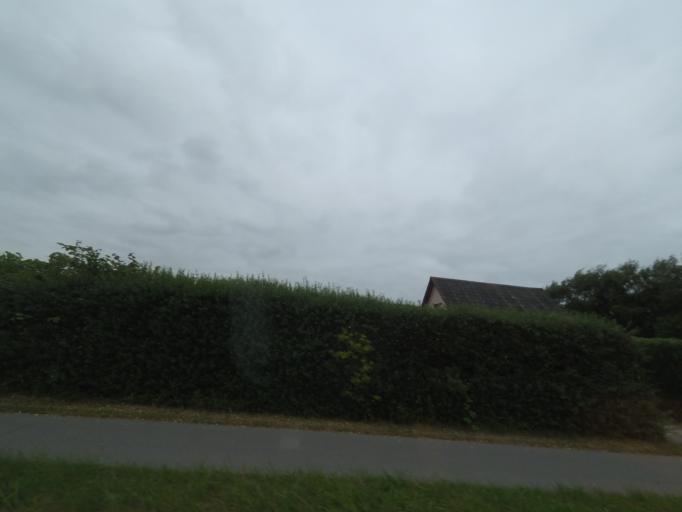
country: DK
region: South Denmark
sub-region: Nordfyns Kommune
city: Otterup
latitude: 55.5376
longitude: 10.4280
